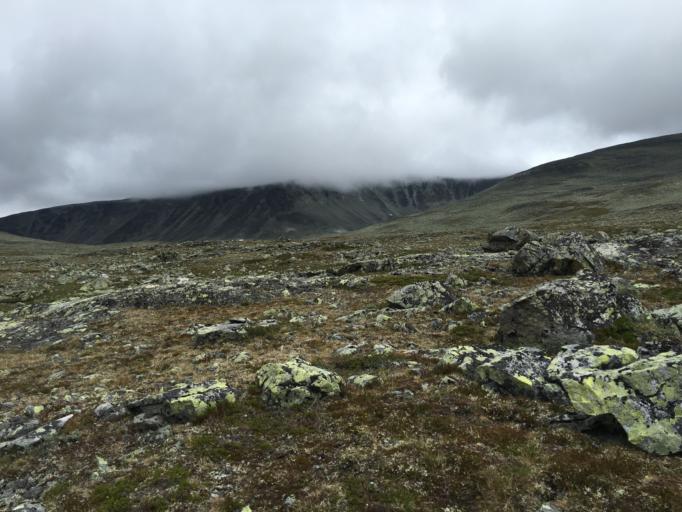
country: NO
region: Oppland
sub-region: Lom
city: Fossbergom
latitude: 61.5852
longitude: 8.7195
